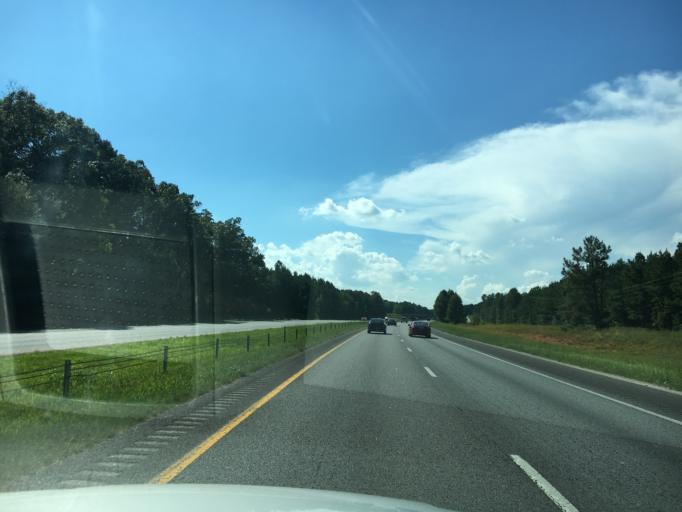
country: US
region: South Carolina
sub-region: Greenville County
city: Fountain Inn
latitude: 34.6392
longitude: -82.1395
